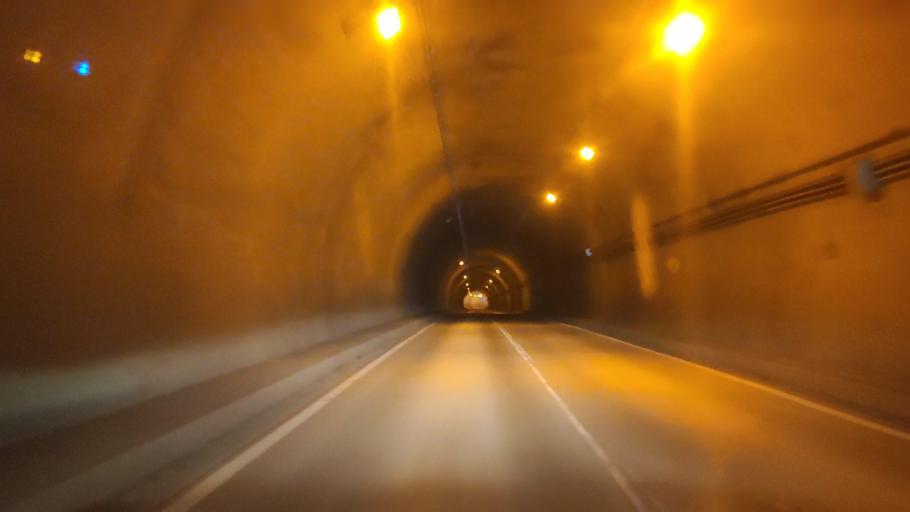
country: JP
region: Kumamoto
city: Hitoyoshi
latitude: 32.4162
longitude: 130.8449
